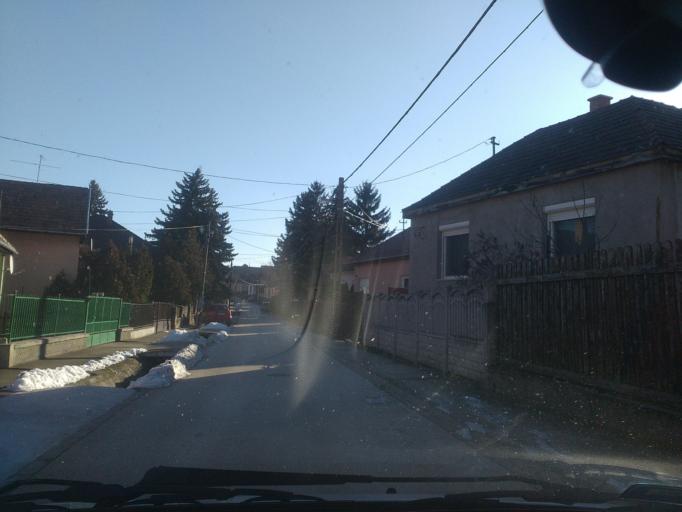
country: HU
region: Pest
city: Pilisvorosvar
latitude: 47.6128
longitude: 18.9075
